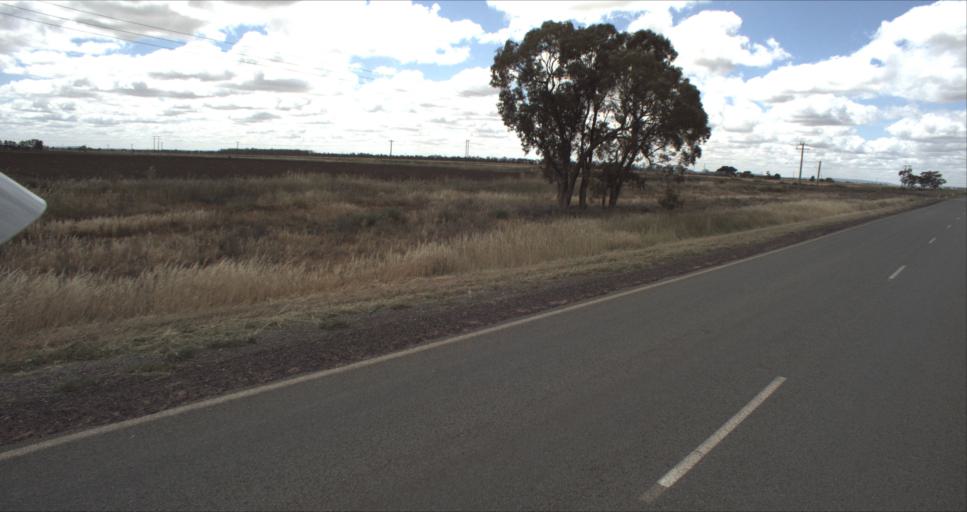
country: AU
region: New South Wales
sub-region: Murrumbidgee Shire
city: Darlington Point
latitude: -34.4958
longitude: 146.1785
